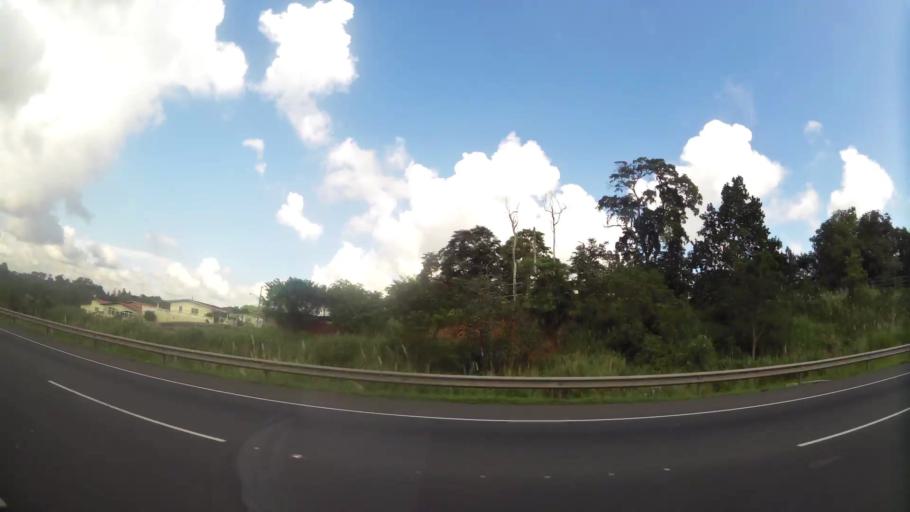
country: PA
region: Panama
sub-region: Distrito Arraijan
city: Arraijan
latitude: 8.9432
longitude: -79.6739
